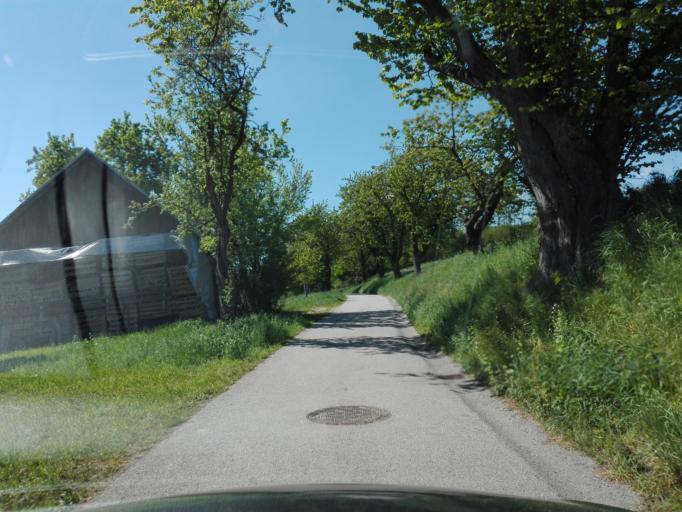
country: AT
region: Upper Austria
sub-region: Politischer Bezirk Urfahr-Umgebung
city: Feldkirchen an der Donau
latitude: 48.3435
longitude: 13.9681
